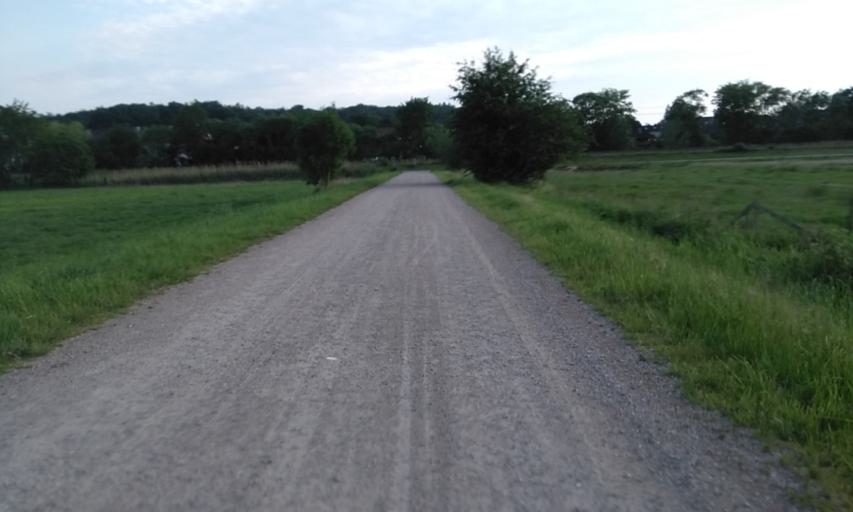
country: DE
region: Lower Saxony
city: Nottensdorf
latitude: 53.4862
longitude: 9.6304
